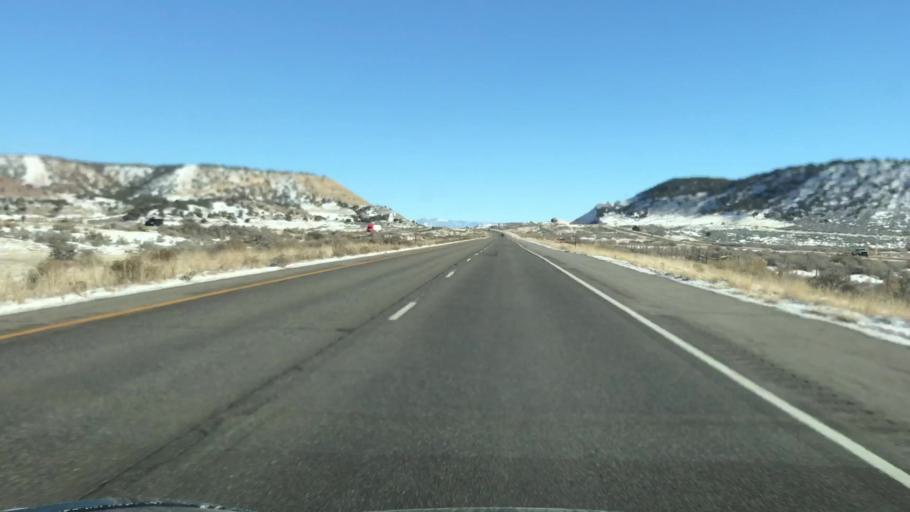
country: US
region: Colorado
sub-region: Garfield County
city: Rifle
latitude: 39.5045
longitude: -107.8935
